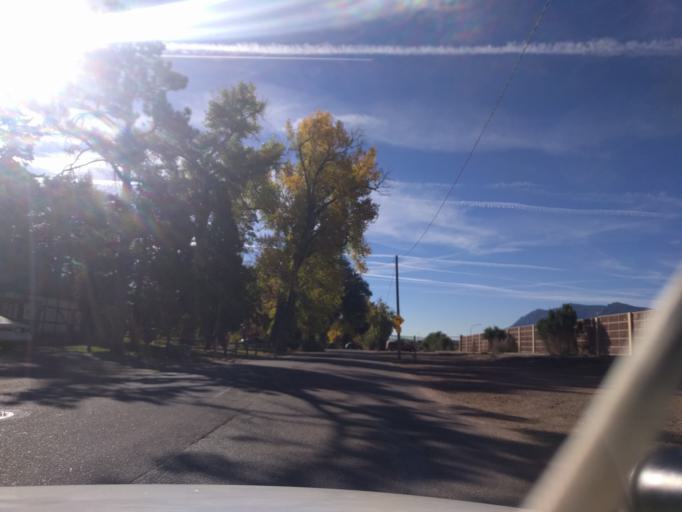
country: US
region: Colorado
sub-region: El Paso County
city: Colorado Springs
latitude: 38.8473
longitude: -104.8302
